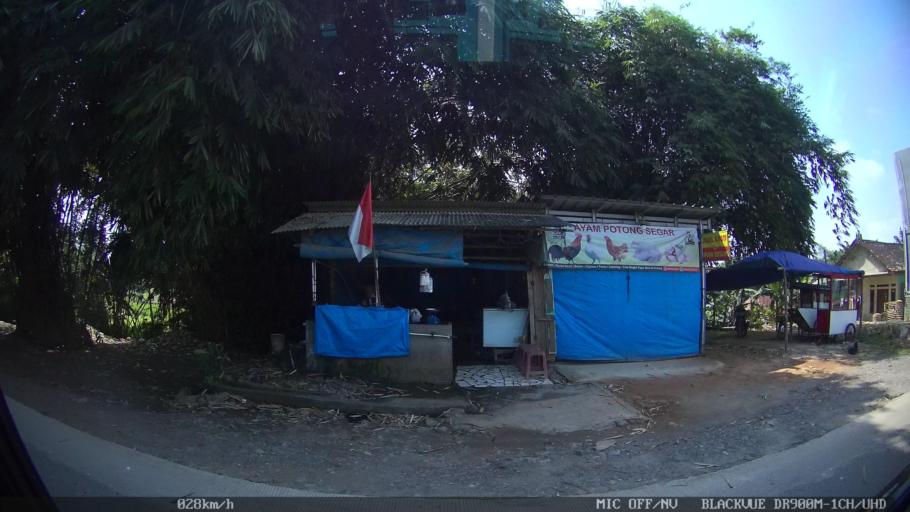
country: ID
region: Lampung
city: Kedaton
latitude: -5.3415
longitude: 105.2722
